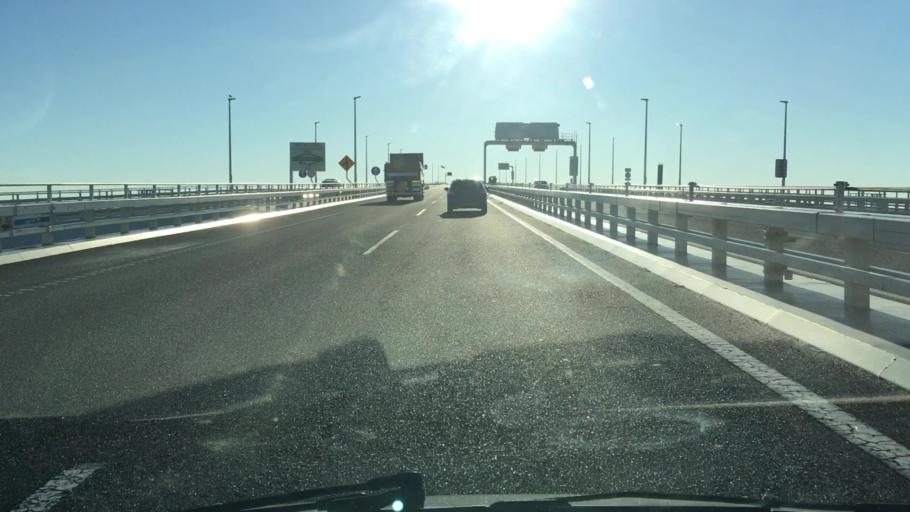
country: JP
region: Chiba
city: Kisarazu
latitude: 35.4612
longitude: 139.8791
